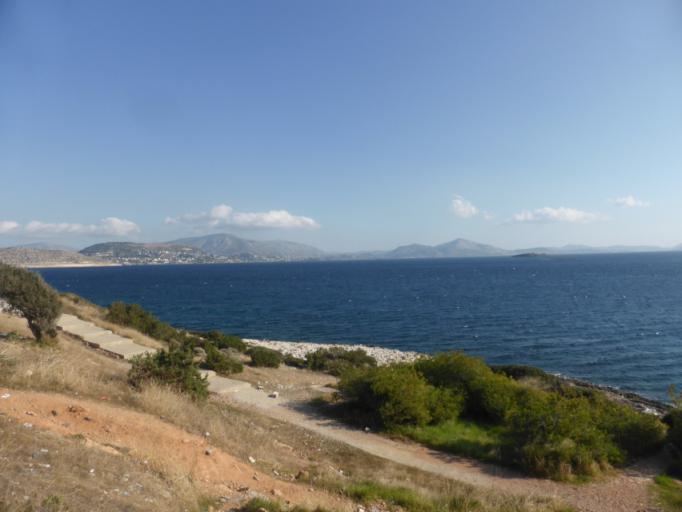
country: GR
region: Attica
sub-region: Nomarchia Anatolikis Attikis
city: Vouliagmeni
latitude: 37.8043
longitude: 23.7982
